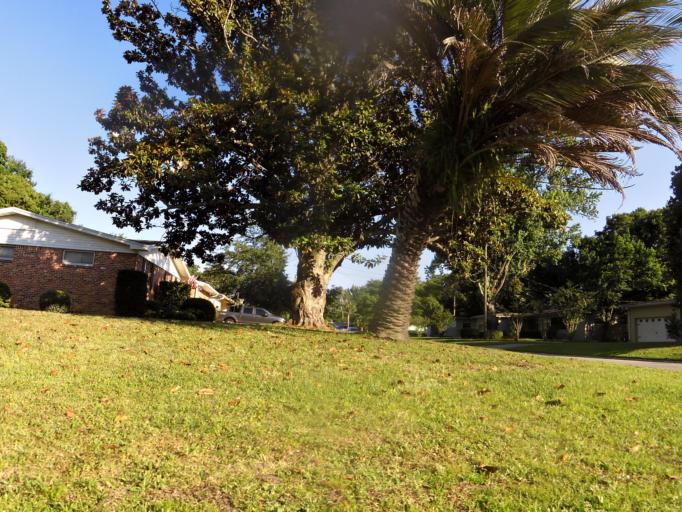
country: US
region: Florida
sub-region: Duval County
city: Jacksonville
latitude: 30.2409
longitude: -81.6145
